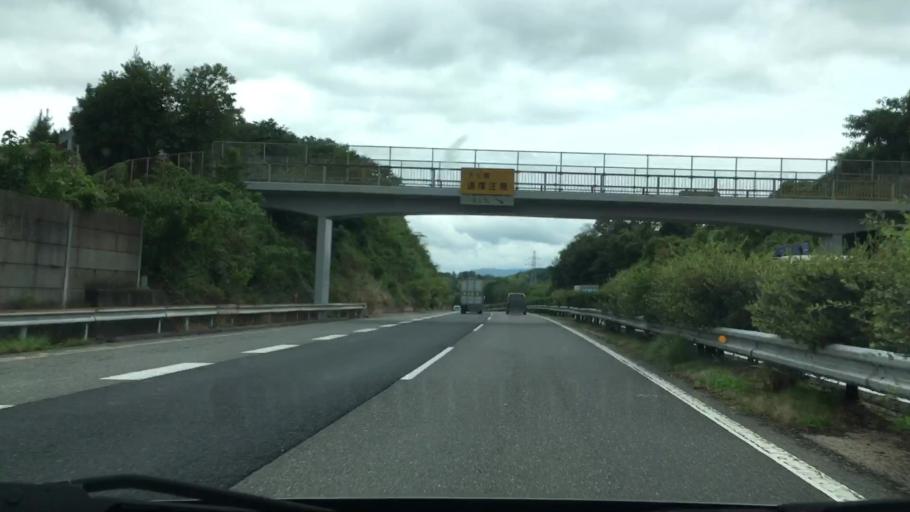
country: JP
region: Okayama
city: Tsuyama
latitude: 35.0649
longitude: 133.9707
